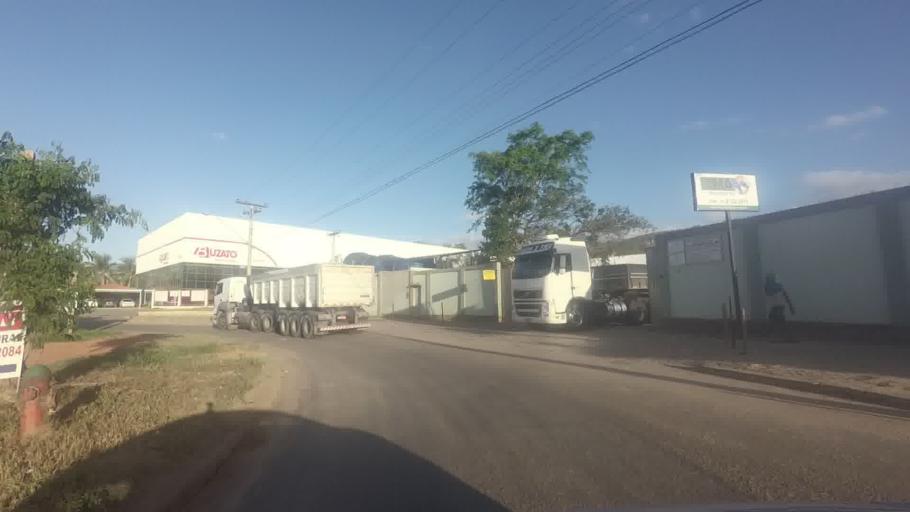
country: BR
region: Espirito Santo
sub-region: Cachoeiro De Itapemirim
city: Cachoeiro de Itapemirim
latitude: -20.8331
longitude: -41.1778
